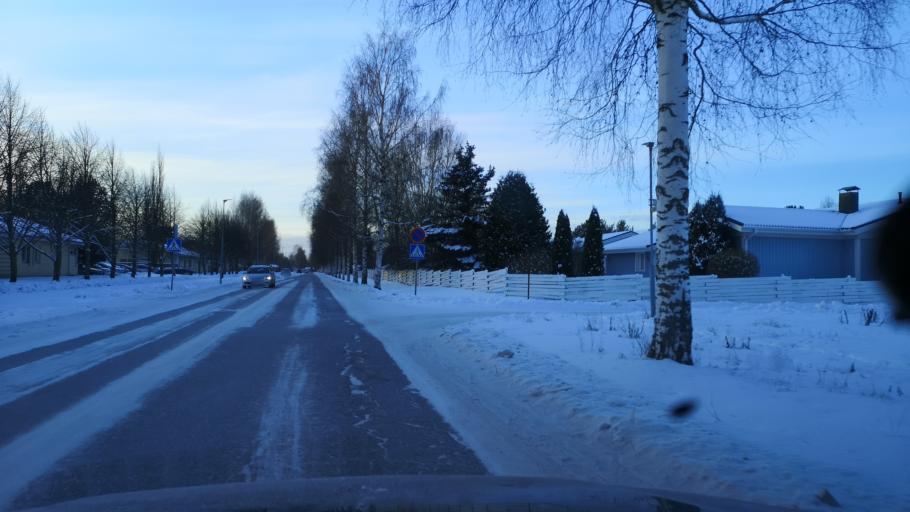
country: FI
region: Satakunta
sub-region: Pori
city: Pori
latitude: 61.5034
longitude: 21.8267
